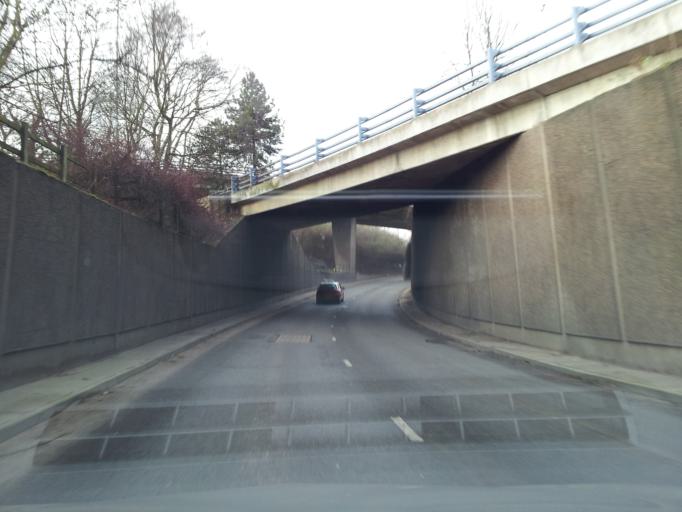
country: GB
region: England
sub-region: Derby
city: Derby
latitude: 52.9246
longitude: -1.4684
